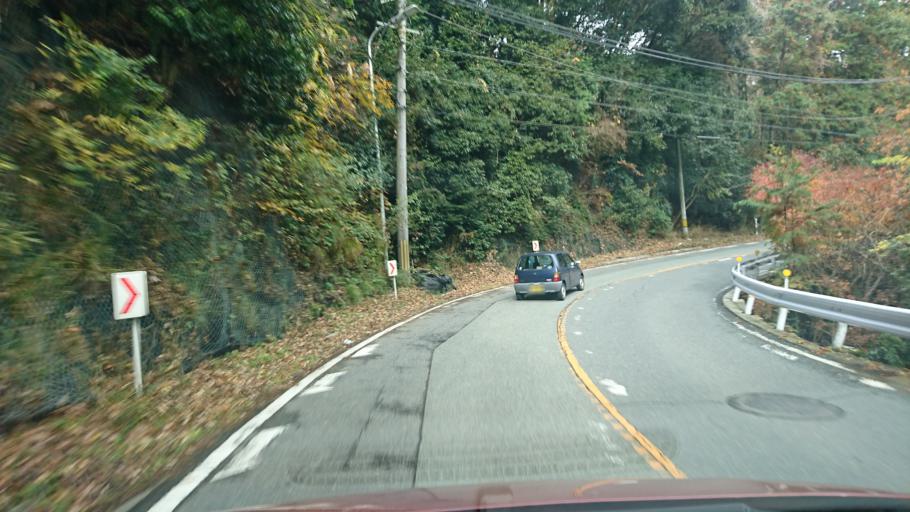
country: JP
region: Osaka
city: Ikeda
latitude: 34.8857
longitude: 135.4269
